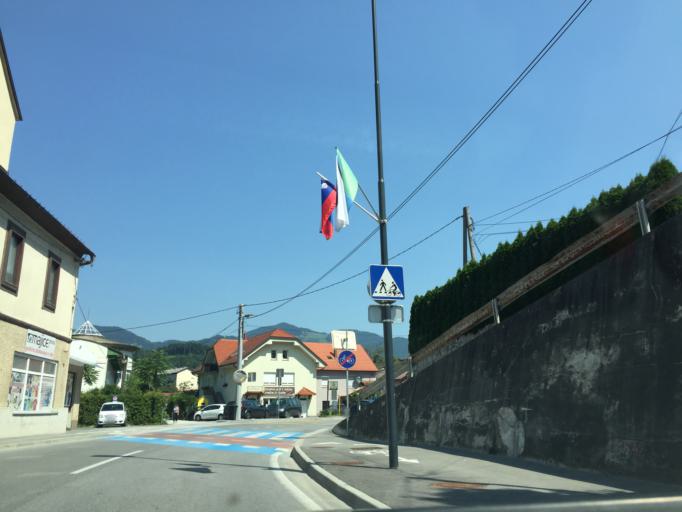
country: SI
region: Zagorje ob Savi
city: Zagorje ob Savi
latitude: 46.1270
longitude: 14.9970
